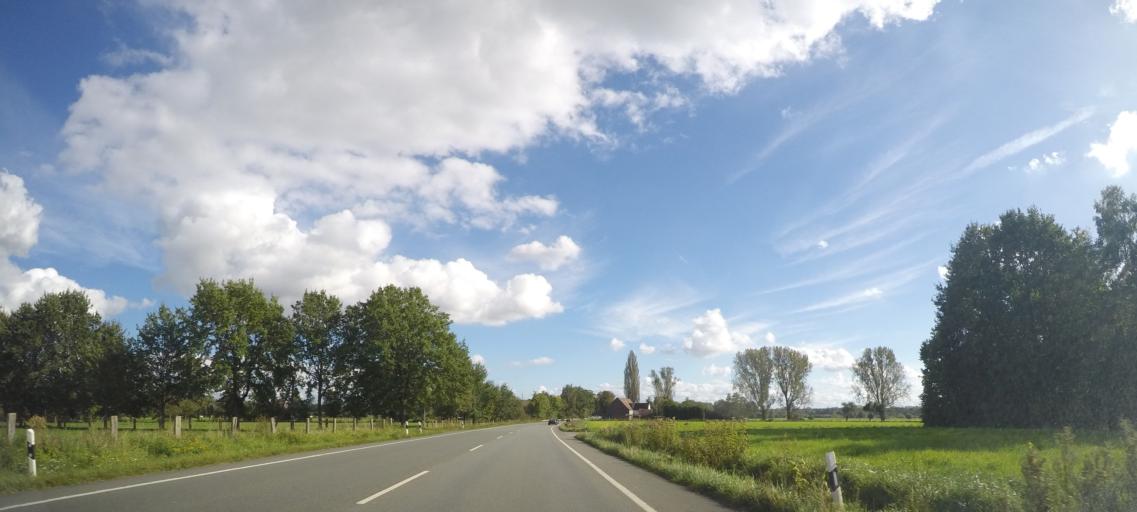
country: DE
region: North Rhine-Westphalia
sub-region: Regierungsbezirk Arnsberg
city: Welver
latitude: 51.6831
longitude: 7.9957
